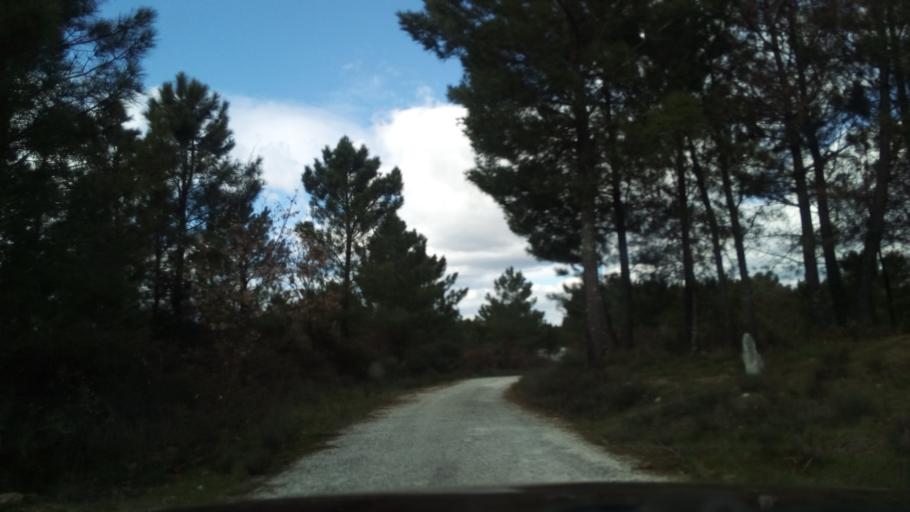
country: PT
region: Guarda
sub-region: Fornos de Algodres
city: Fornos de Algodres
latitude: 40.6673
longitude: -7.5019
